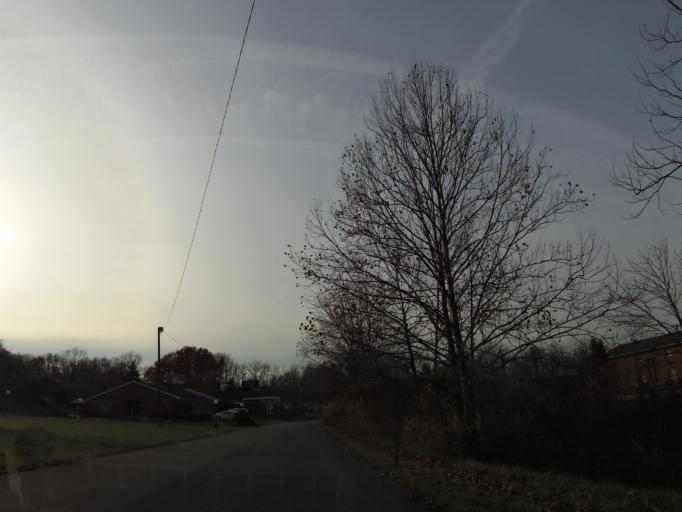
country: US
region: Kentucky
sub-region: Harrison County
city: Cynthiana
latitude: 38.3939
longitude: -84.2820
